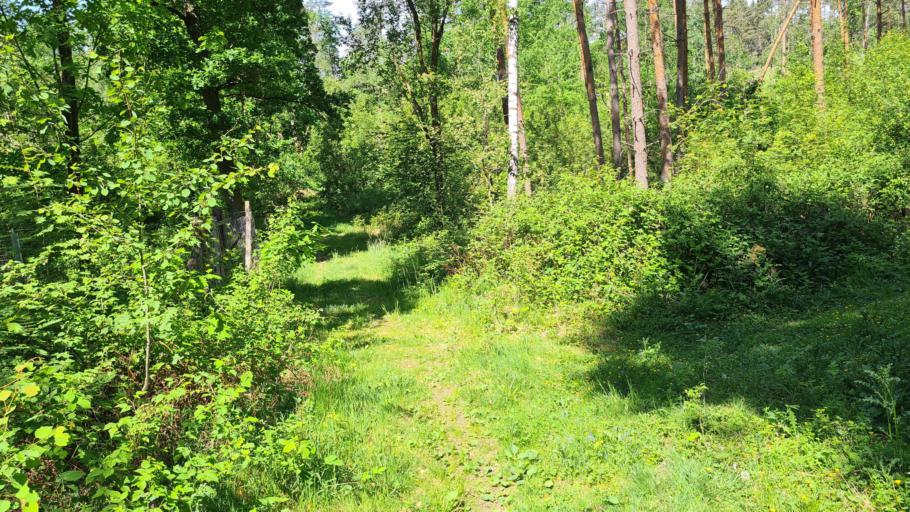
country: DE
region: Brandenburg
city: Grosskmehlen
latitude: 51.3621
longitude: 13.7152
